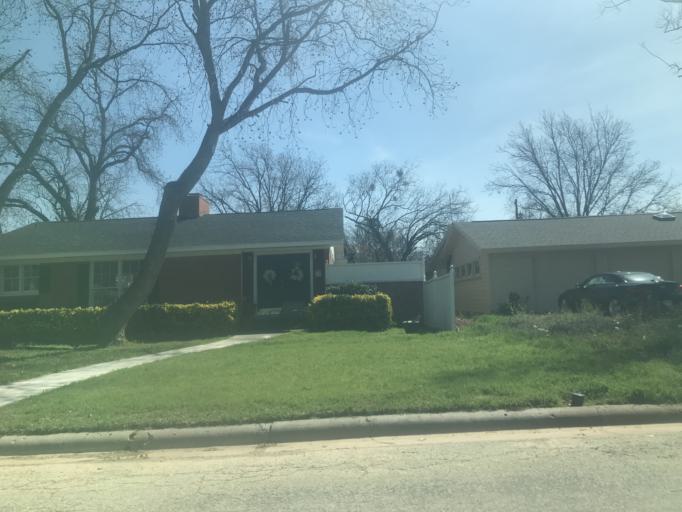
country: US
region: Texas
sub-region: Taylor County
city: Abilene
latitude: 32.4374
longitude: -99.7764
